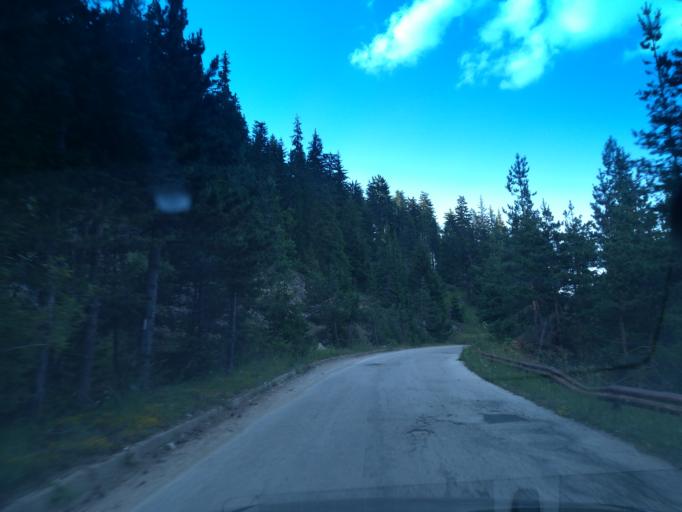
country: BG
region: Smolyan
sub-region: Obshtina Chepelare
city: Chepelare
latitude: 41.6884
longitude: 24.7577
